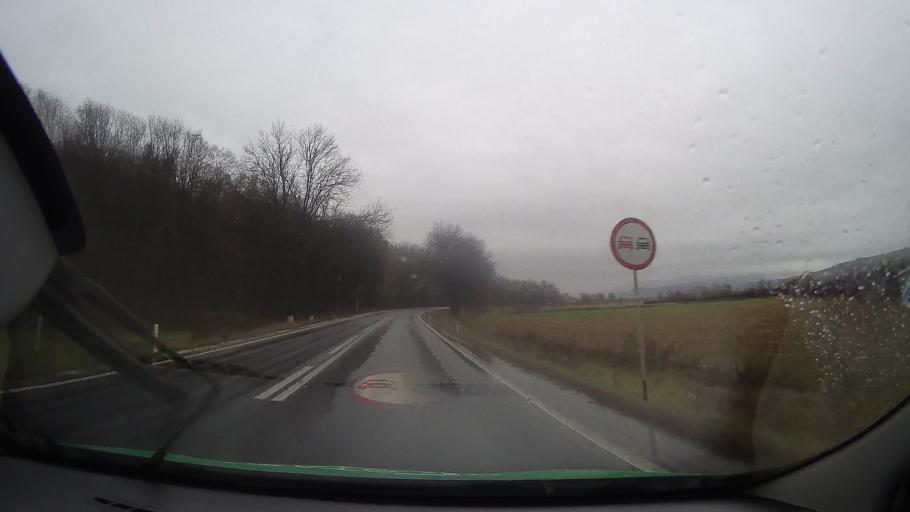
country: RO
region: Mures
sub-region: Comuna Brancovenesti
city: Valenii de Mures
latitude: 46.8786
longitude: 24.7779
